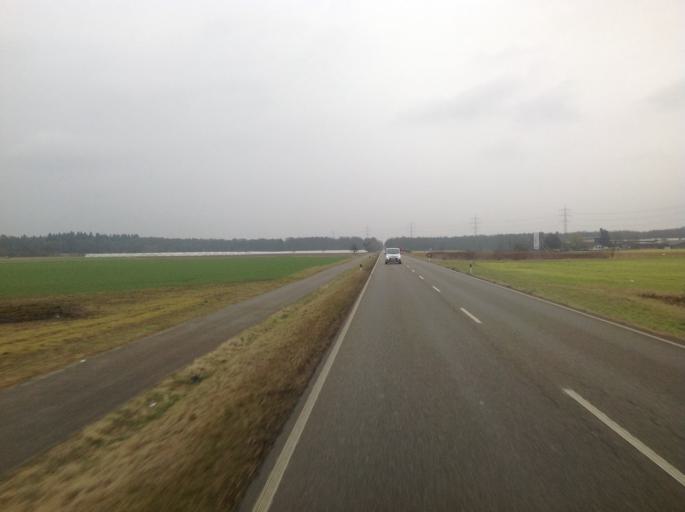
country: DE
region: Baden-Wuerttemberg
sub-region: Karlsruhe Region
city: Iffezheim
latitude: 48.8212
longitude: 8.1589
